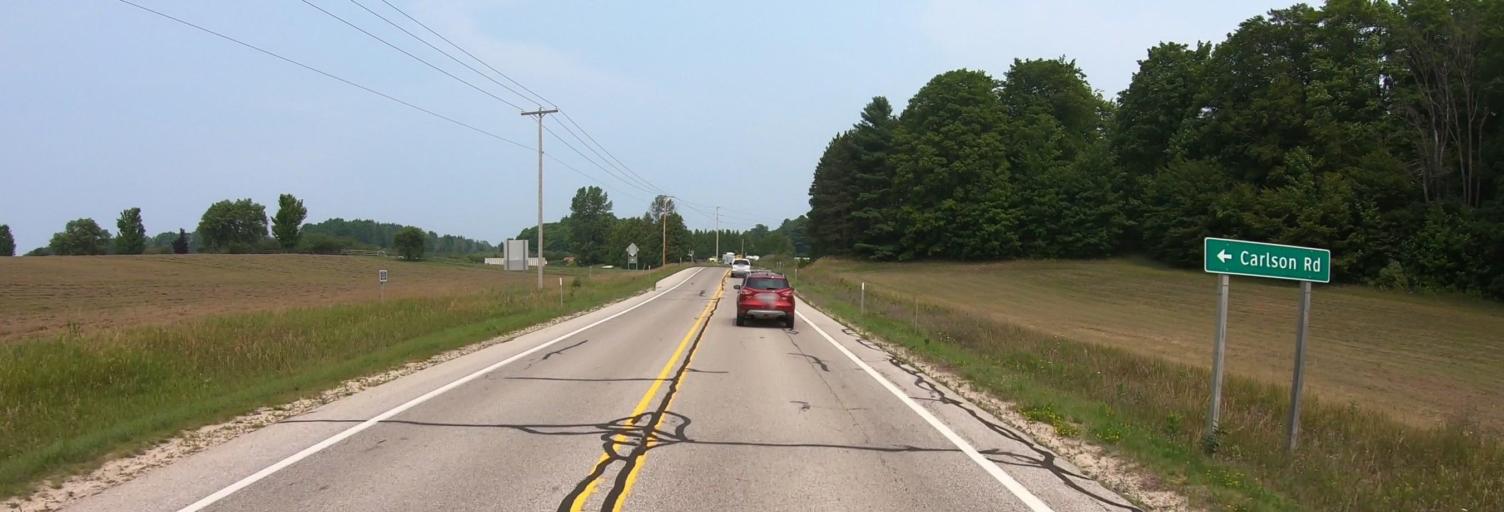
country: US
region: Michigan
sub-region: Leelanau County
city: Leland
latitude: 45.0974
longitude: -85.6600
